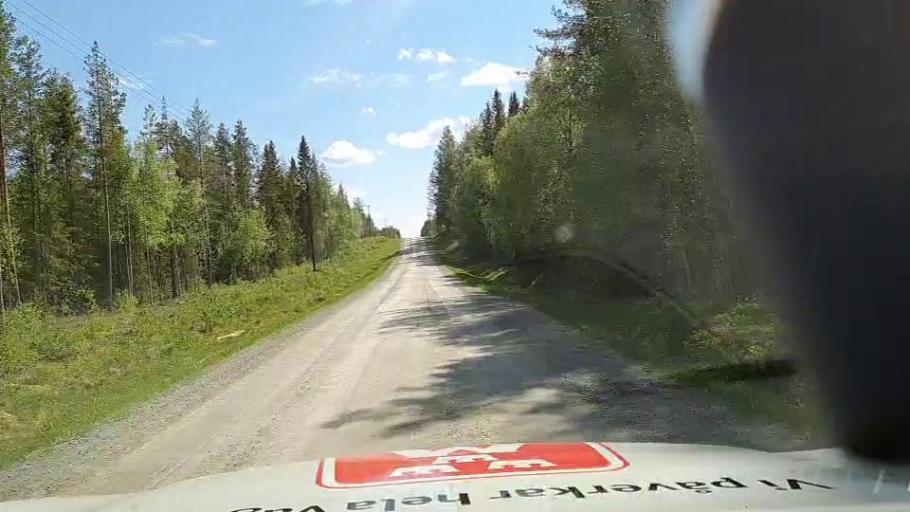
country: SE
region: Jaemtland
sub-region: Stroemsunds Kommun
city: Stroemsund
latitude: 64.4800
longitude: 15.5926
